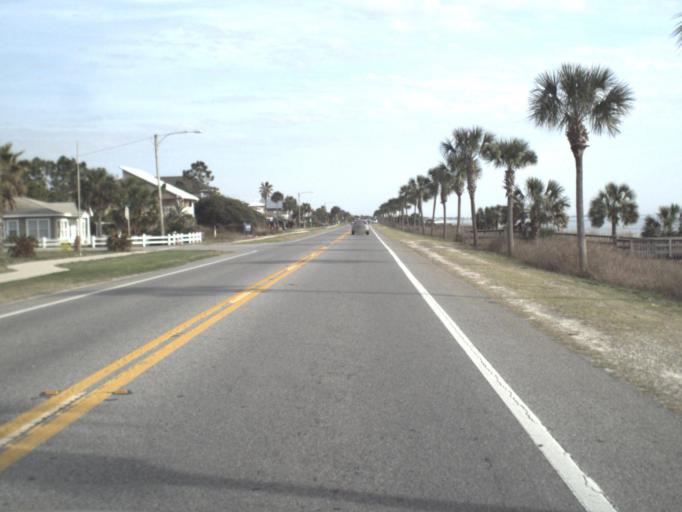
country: US
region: Florida
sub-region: Bay County
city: Mexico Beach
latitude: 29.9350
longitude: -85.4000
